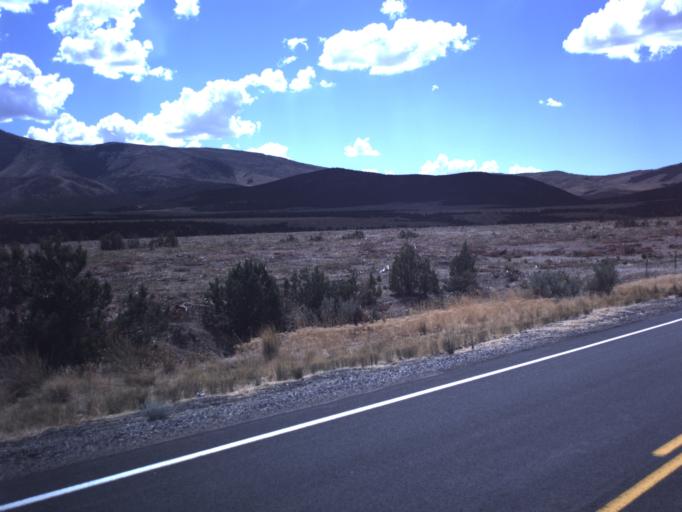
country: US
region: Utah
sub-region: Tooele County
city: Grantsville
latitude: 40.3361
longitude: -112.5050
